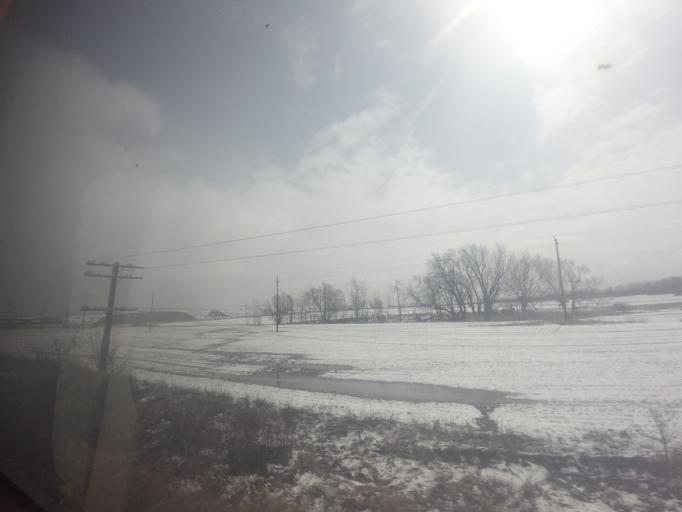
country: CA
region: Ontario
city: Cobourg
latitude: 43.9166
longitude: -78.4647
